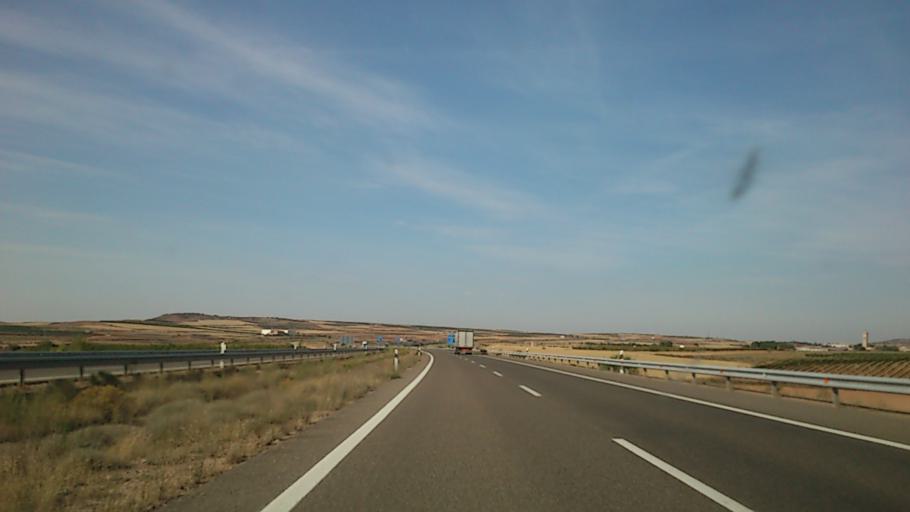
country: ES
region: Aragon
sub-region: Provincia de Zaragoza
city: Longares
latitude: 41.3929
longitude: -1.1818
